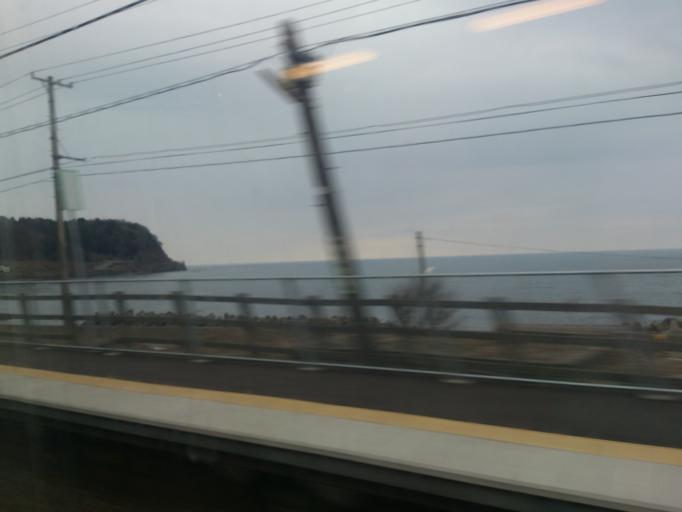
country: JP
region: Niigata
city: Joetsu
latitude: 37.1634
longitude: 138.1376
